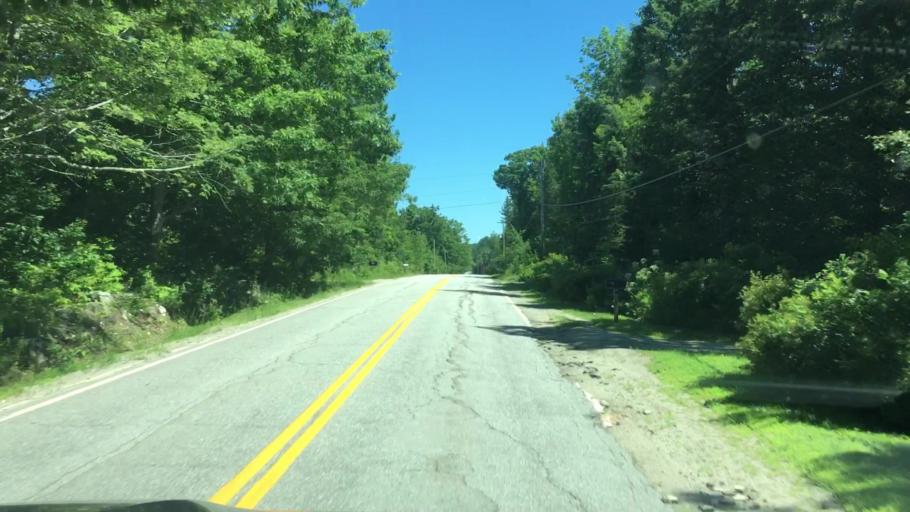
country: US
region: Maine
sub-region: Hancock County
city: Penobscot
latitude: 44.5012
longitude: -68.6803
